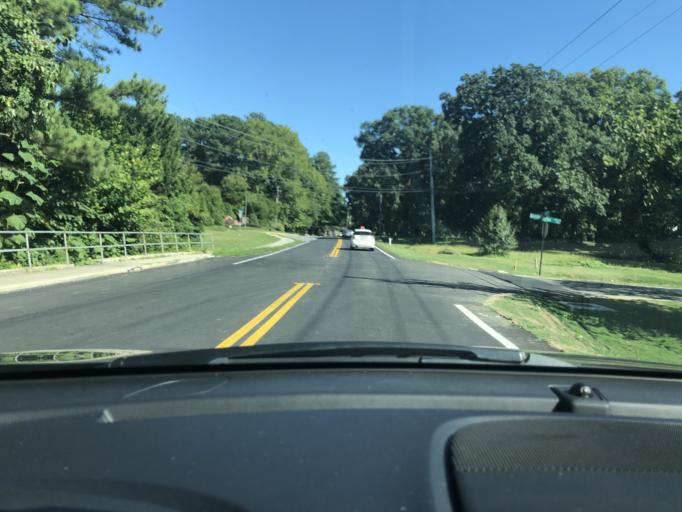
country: US
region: Georgia
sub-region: Gwinnett County
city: Lawrenceville
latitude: 33.9448
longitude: -83.9720
